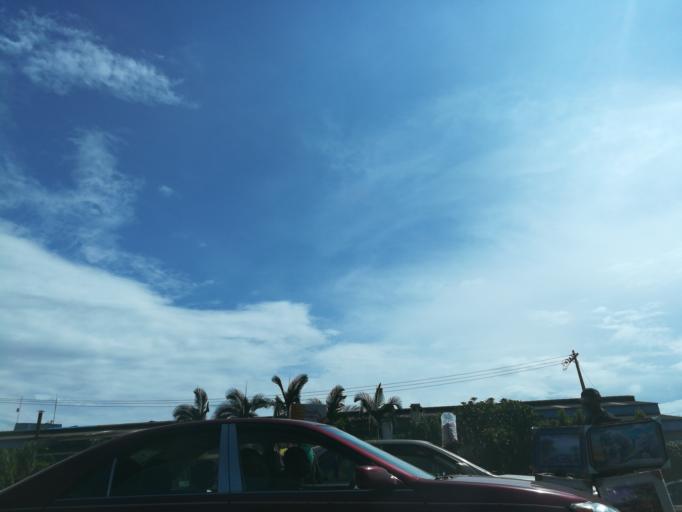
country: NG
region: Lagos
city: Agege
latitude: 6.6070
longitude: 3.3120
